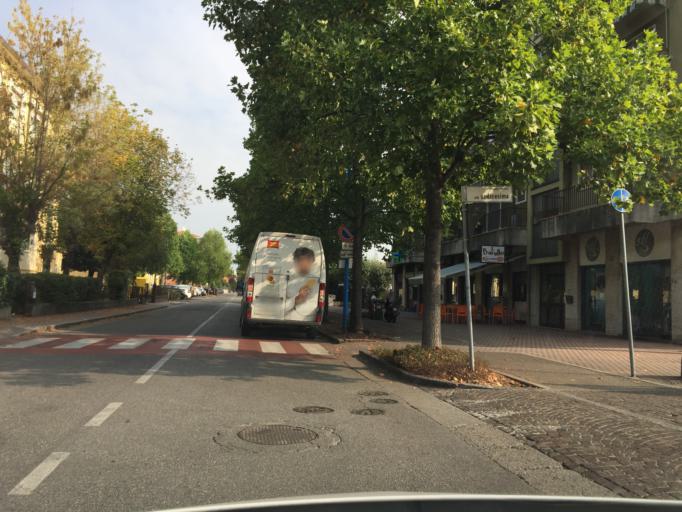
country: IT
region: Lombardy
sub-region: Provincia di Brescia
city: Folzano
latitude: 45.5098
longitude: 10.1868
